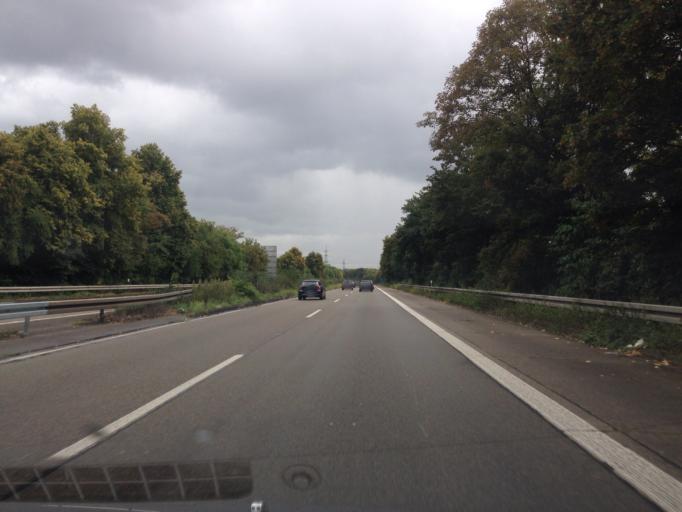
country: DE
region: North Rhine-Westphalia
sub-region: Regierungsbezirk Koln
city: Ostheim
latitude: 50.9117
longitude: 7.0356
